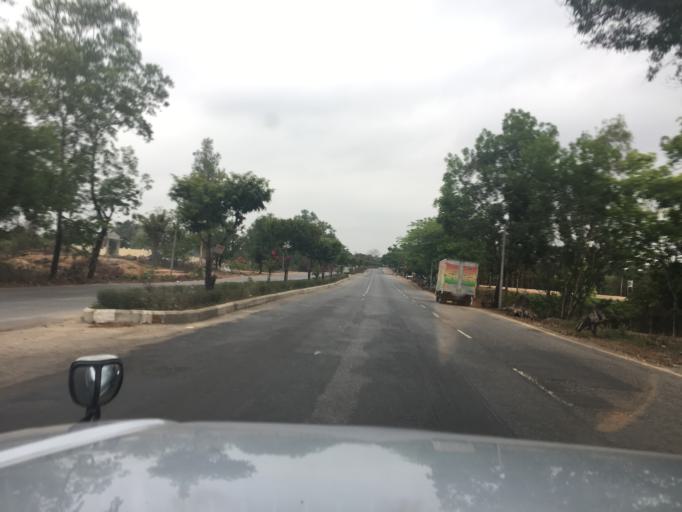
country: MM
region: Bago
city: Thanatpin
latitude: 17.2030
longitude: 96.4116
